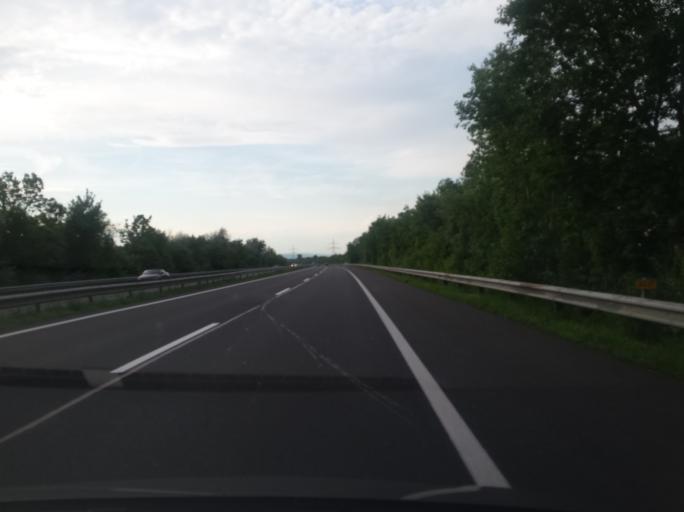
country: AT
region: Burgenland
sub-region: Eisenstadt-Umgebung
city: Wimpassing an der Leitha
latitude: 47.9144
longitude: 16.4073
